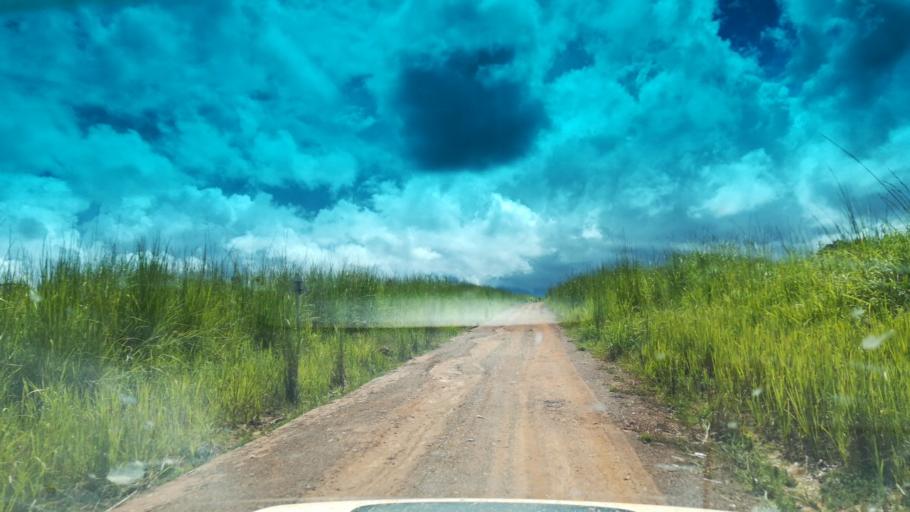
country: ZM
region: Northern
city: Kaputa
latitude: -7.7587
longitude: 29.2329
